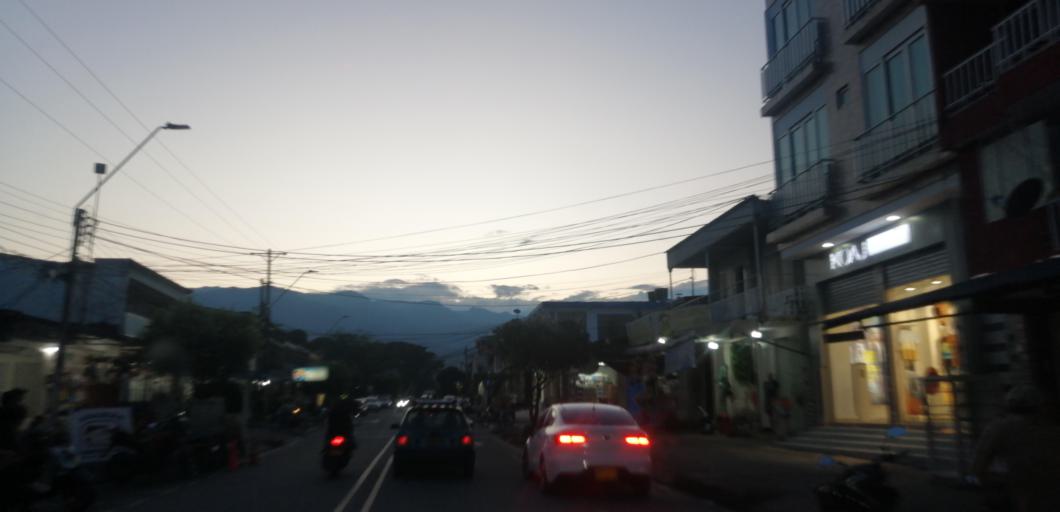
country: CO
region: Meta
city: Acacias
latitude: 3.9883
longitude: -73.7755
